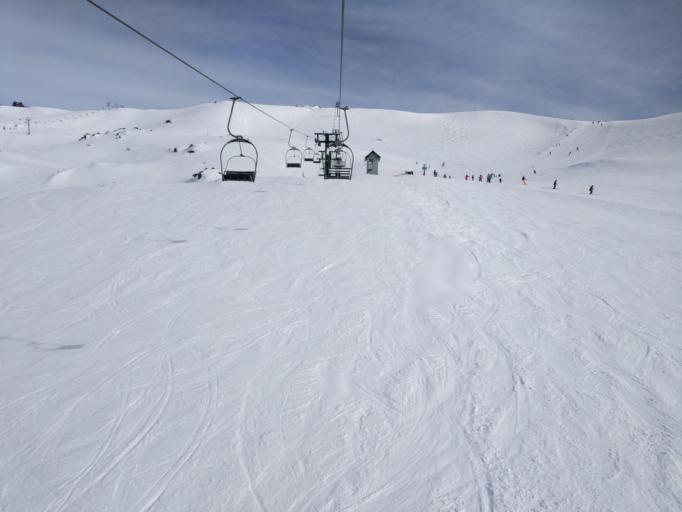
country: AR
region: Rio Negro
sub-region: Departamento de Bariloche
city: San Carlos de Bariloche
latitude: -41.1602
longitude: -71.4705
